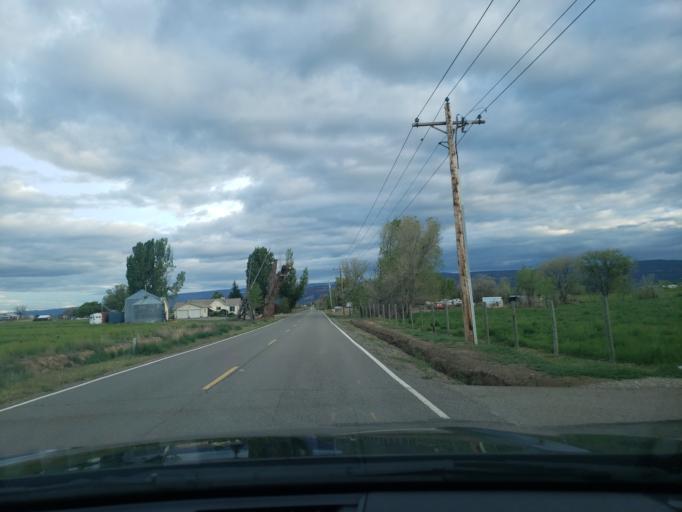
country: US
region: Colorado
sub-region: Mesa County
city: Fruita
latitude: 39.2105
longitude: -108.7011
